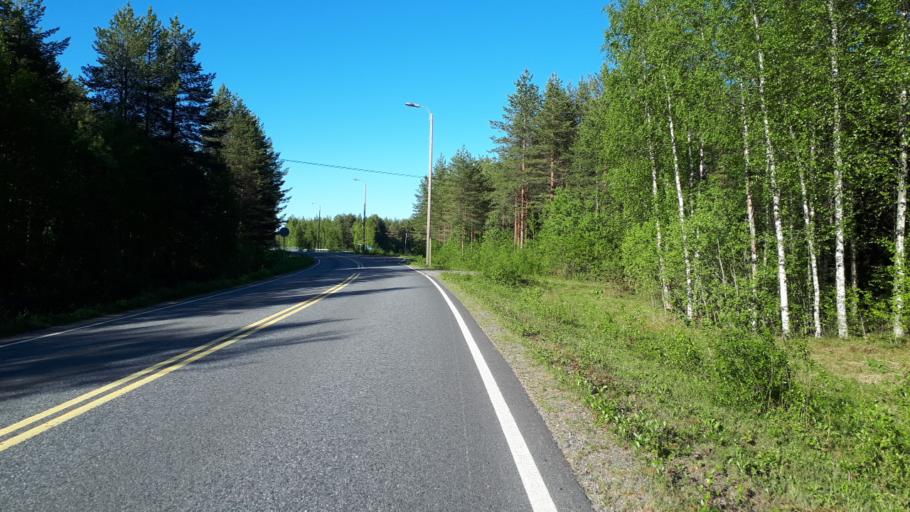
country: FI
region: Northern Ostrobothnia
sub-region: Oulunkaari
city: Ii
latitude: 65.3259
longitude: 25.5179
